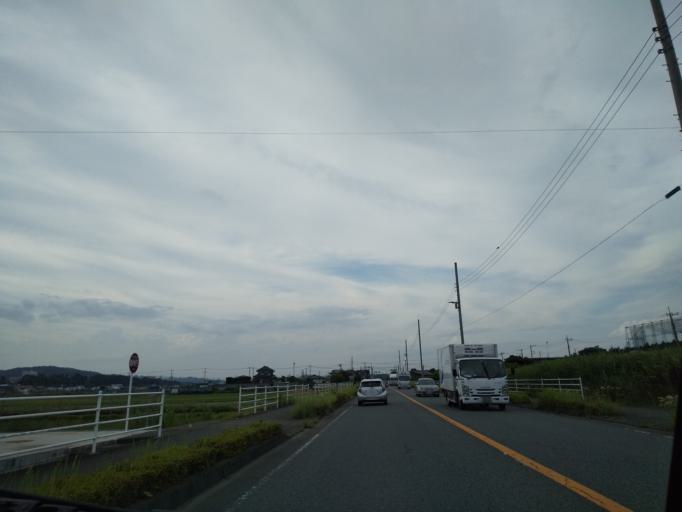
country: JP
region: Kanagawa
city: Atsugi
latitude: 35.4706
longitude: 139.3588
